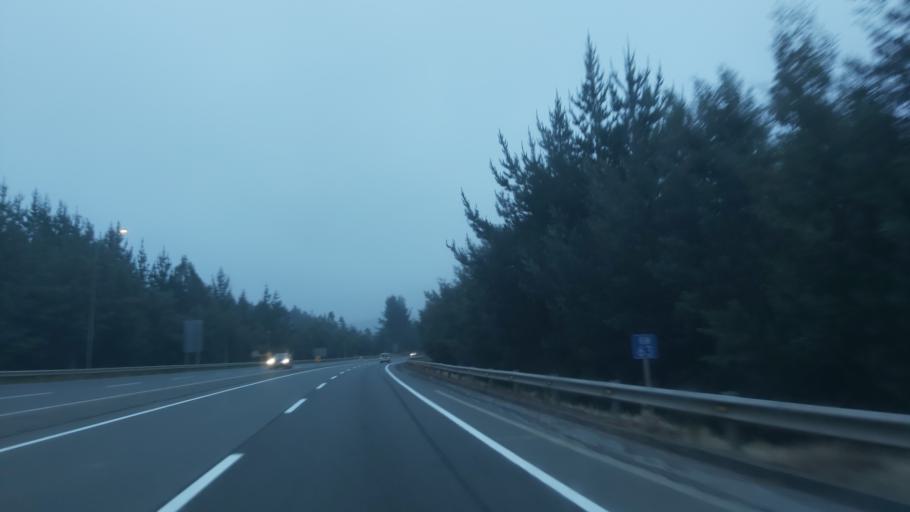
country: CL
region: Biobio
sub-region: Provincia de Concepcion
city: Penco
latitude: -36.7370
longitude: -72.8911
